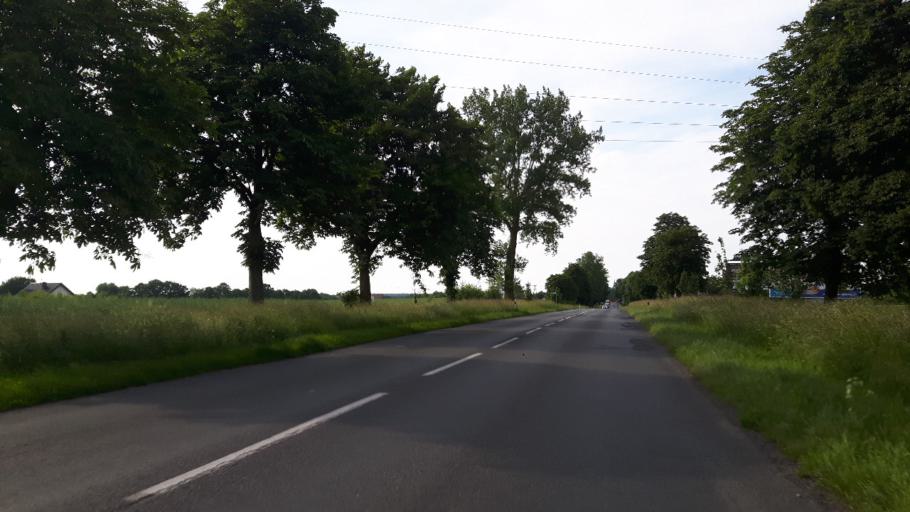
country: PL
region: West Pomeranian Voivodeship
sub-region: Powiat gryficki
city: Gryfice
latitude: 53.8982
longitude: 15.2046
